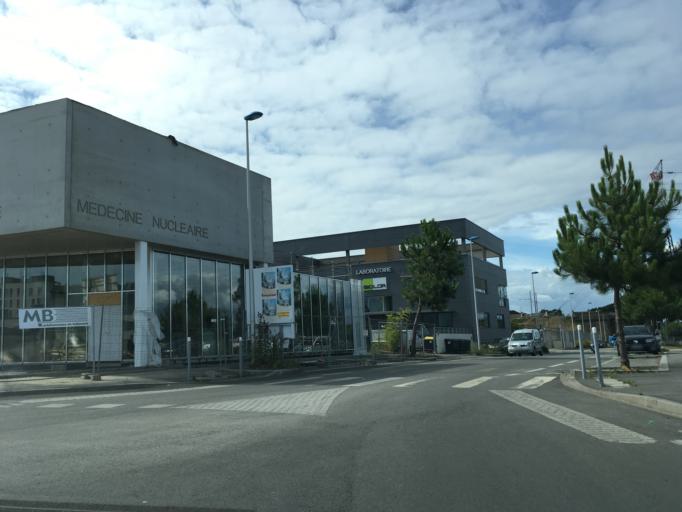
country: FR
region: Brittany
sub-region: Departement du Morbihan
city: Lorient
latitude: 47.7551
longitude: -3.3546
